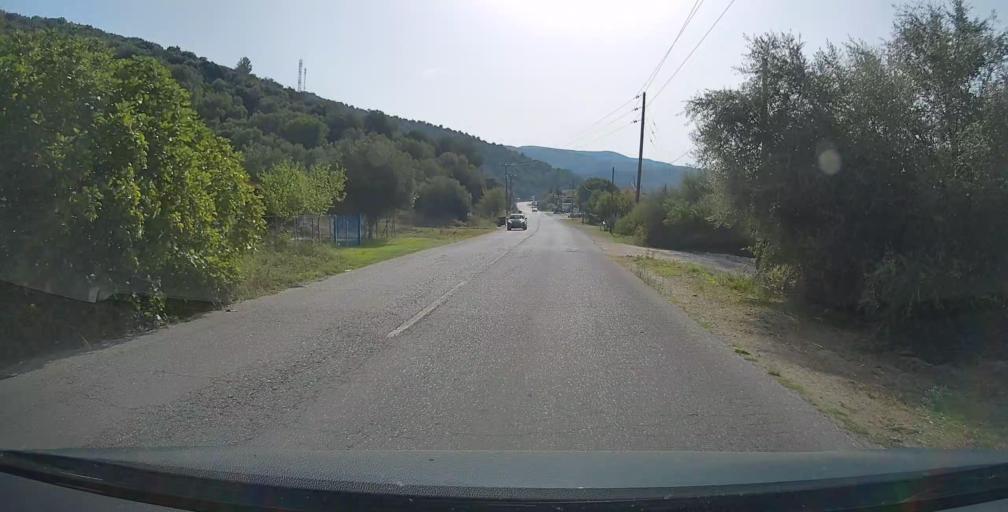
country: GR
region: Central Macedonia
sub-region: Nomos Chalkidikis
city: Sykia
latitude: 39.9732
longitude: 23.9143
